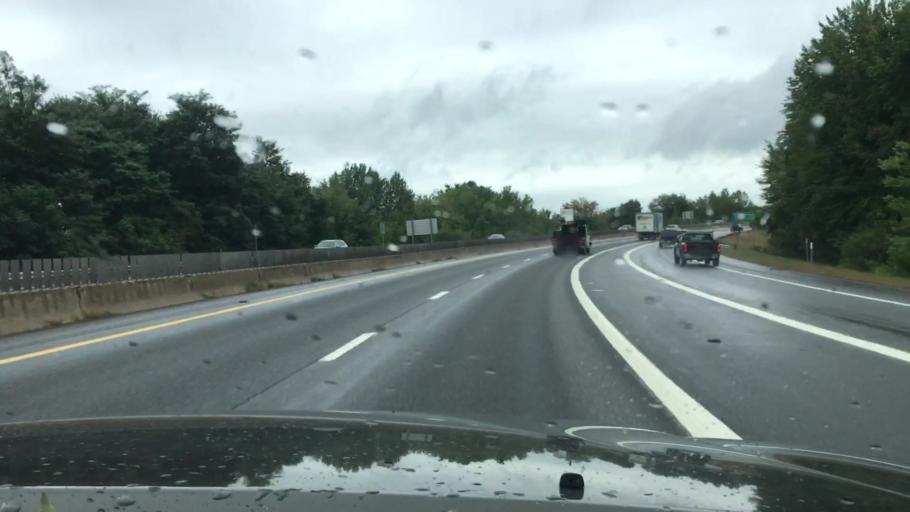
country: US
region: New Hampshire
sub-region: Merrimack County
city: Concord
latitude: 43.1874
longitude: -71.5228
